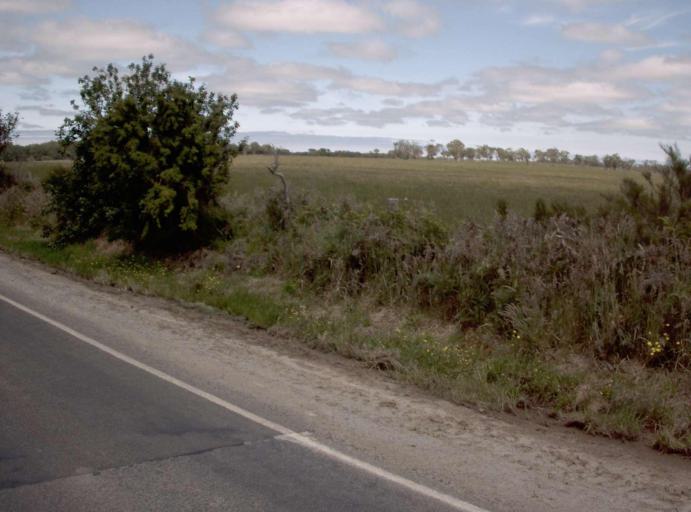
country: AU
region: Victoria
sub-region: Bass Coast
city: North Wonthaggi
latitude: -38.6428
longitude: 146.0105
